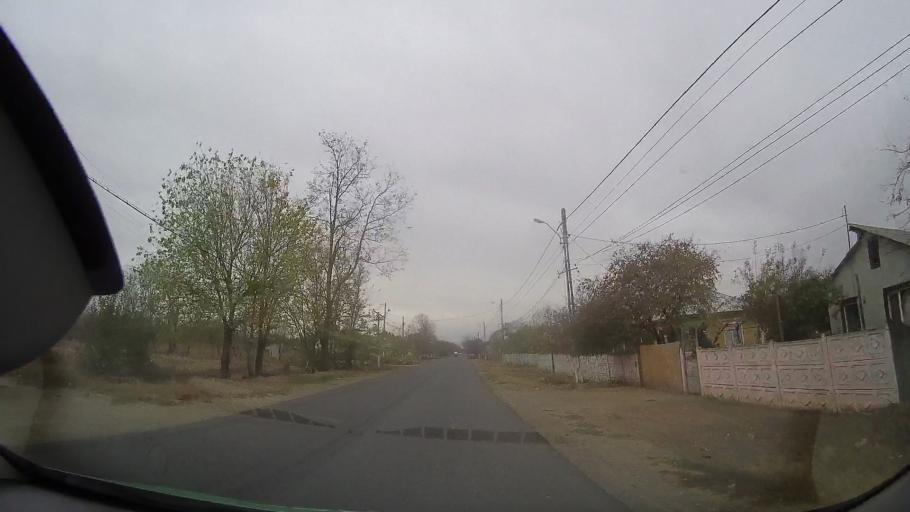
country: RO
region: Braila
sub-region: Comuna Ulmu
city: Ulmu
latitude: 44.9510
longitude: 27.3184
